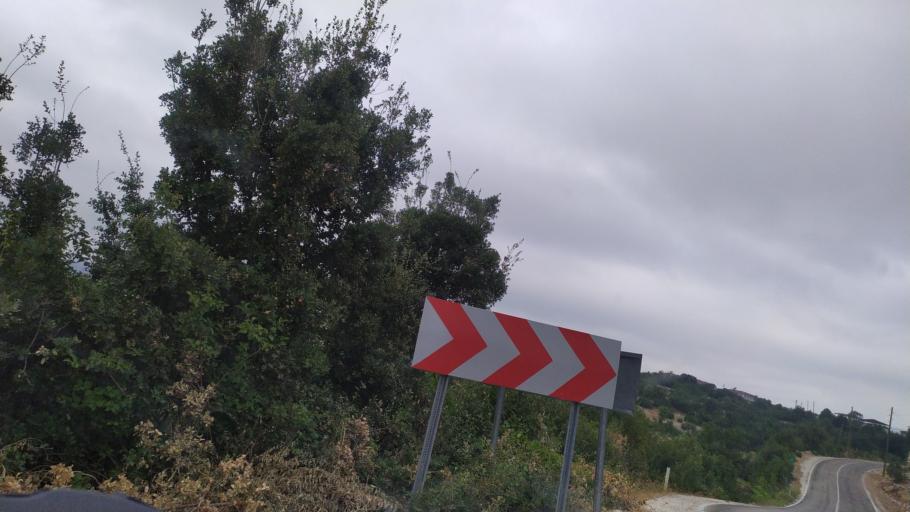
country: TR
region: Mersin
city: Silifke
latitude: 36.5502
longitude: 33.9177
